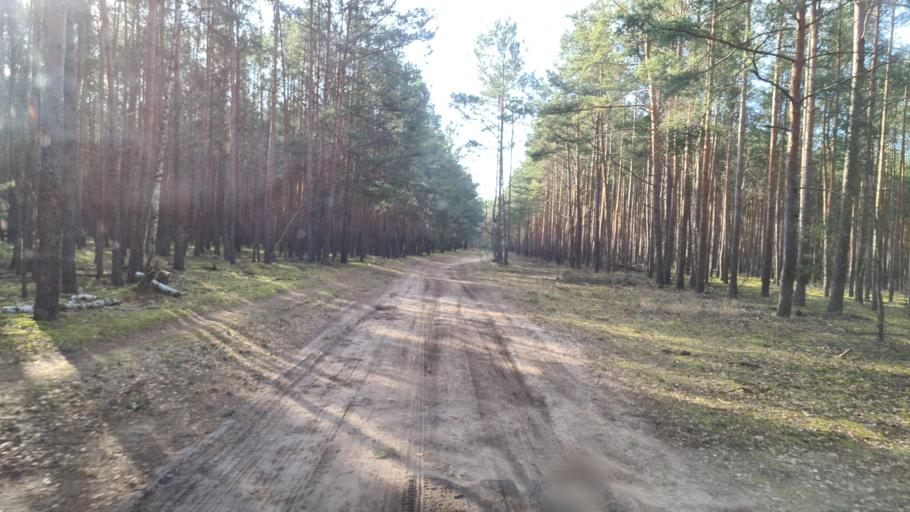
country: DE
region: Brandenburg
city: Gross Koris
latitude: 52.1551
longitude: 13.6926
